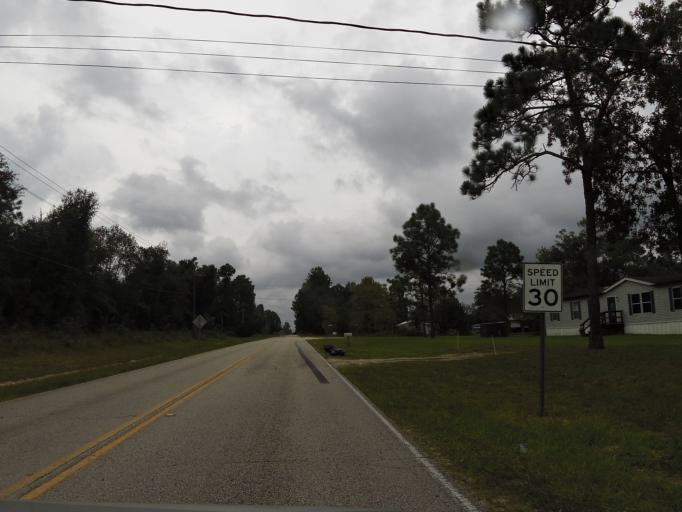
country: US
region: Florida
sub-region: Clay County
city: Middleburg
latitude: 30.0942
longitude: -81.9490
